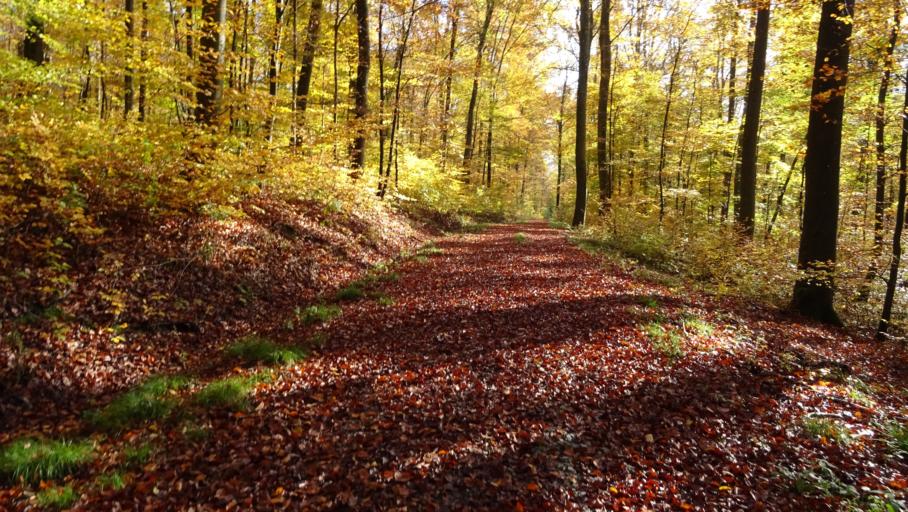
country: DE
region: Baden-Wuerttemberg
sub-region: Karlsruhe Region
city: Obrigheim
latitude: 49.3725
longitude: 9.0964
